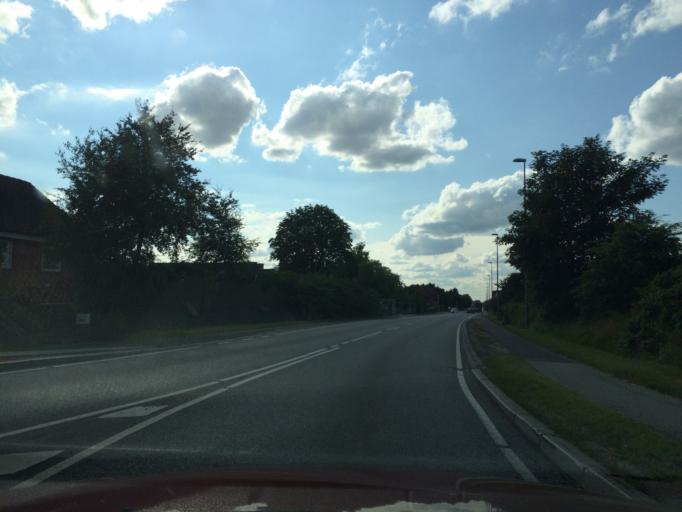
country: DK
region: Central Jutland
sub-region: Favrskov Kommune
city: Hammel
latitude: 56.2378
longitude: 9.8188
